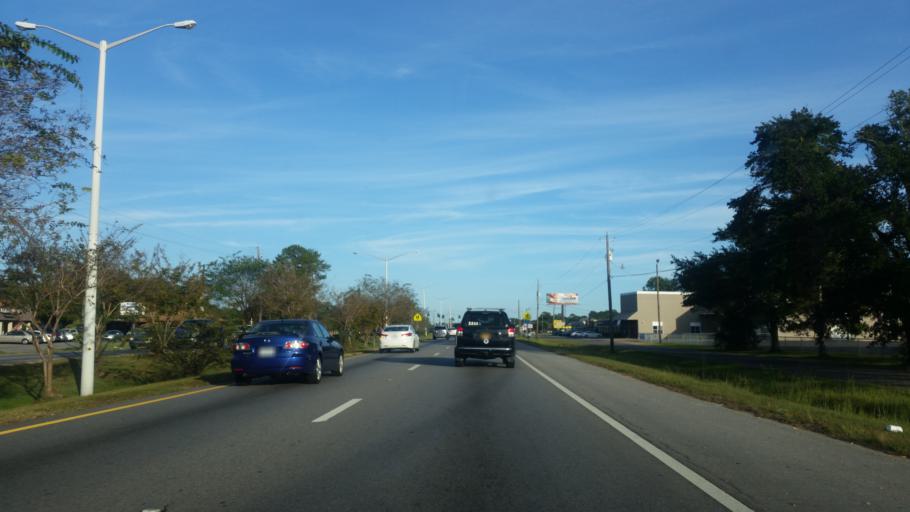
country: US
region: Mississippi
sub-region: Jackson County
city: Ocean Springs
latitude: 30.4145
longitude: -88.7945
